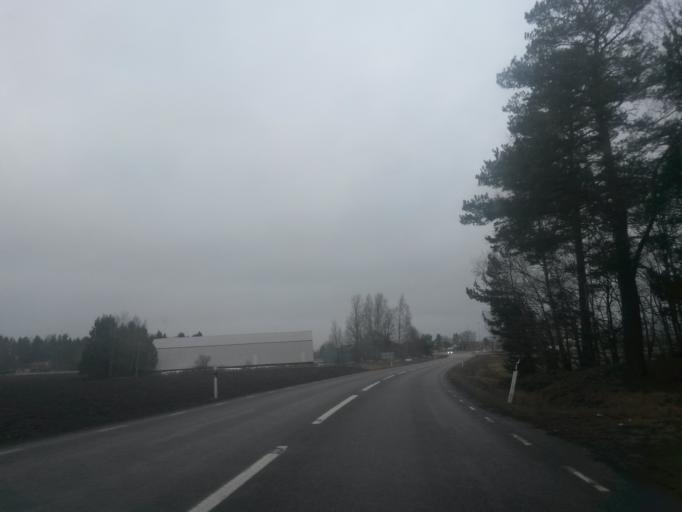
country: SE
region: Vaestra Goetaland
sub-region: Vanersborgs Kommun
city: Vargon
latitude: 58.2608
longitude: 12.4021
